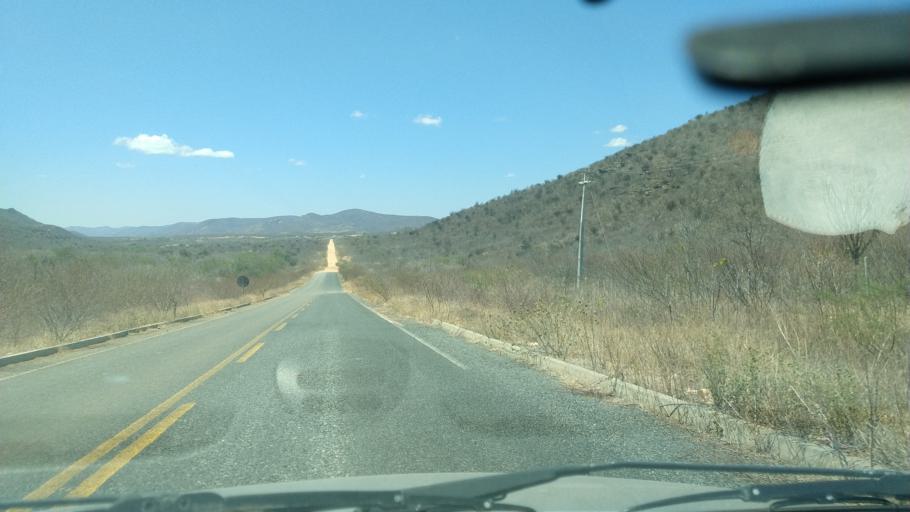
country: BR
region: Rio Grande do Norte
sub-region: Sao Tome
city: Sao Tome
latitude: -5.9676
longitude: -36.1585
